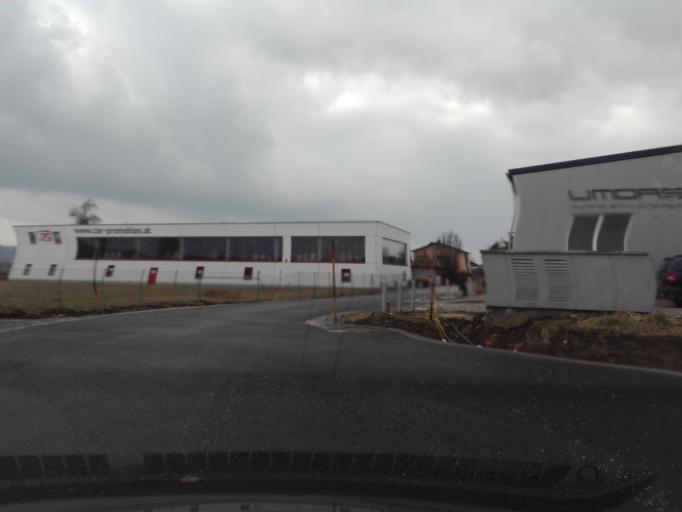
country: AT
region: Upper Austria
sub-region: Politischer Bezirk Urfahr-Umgebung
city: Goldworth
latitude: 48.2896
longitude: 14.1253
